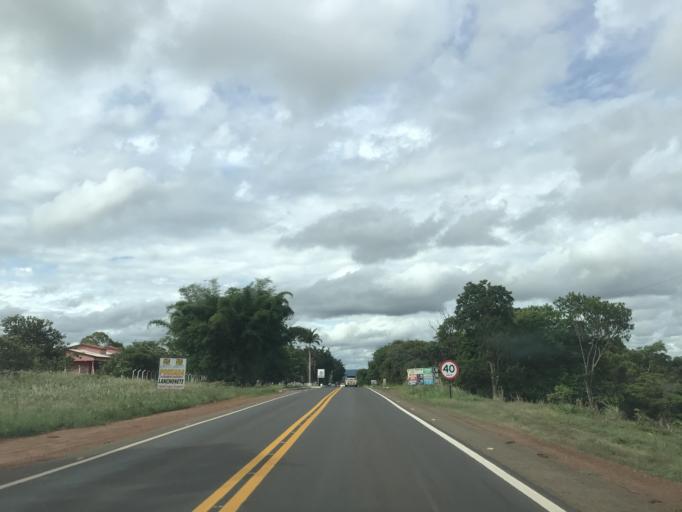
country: BR
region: Goias
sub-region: Piracanjuba
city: Piracanjuba
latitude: -17.2177
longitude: -48.7104
